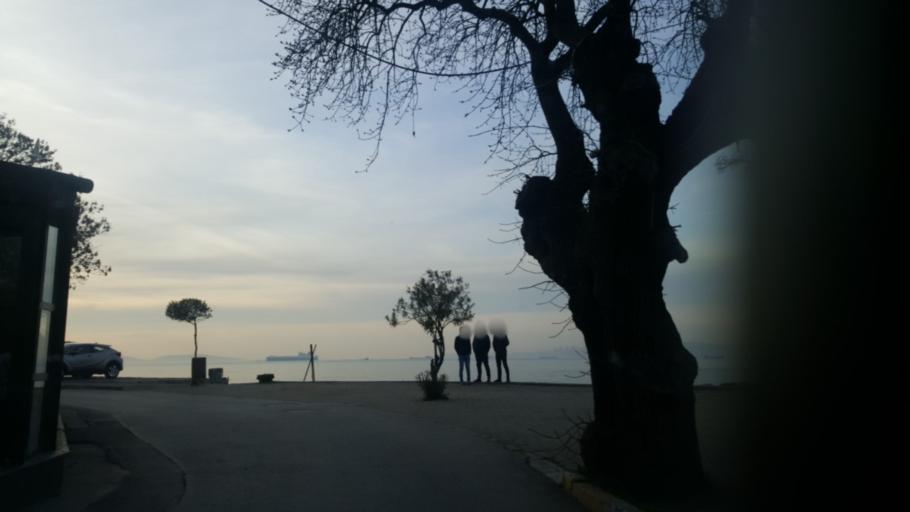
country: TR
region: Istanbul
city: Icmeler
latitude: 40.8200
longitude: 29.2733
